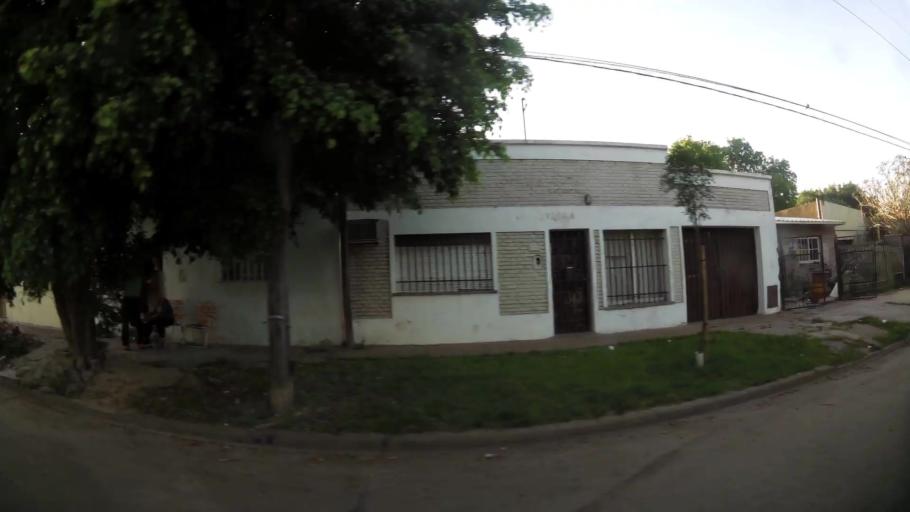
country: AR
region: Santa Fe
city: Santa Fe de la Vera Cruz
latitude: -31.6023
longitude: -60.6898
